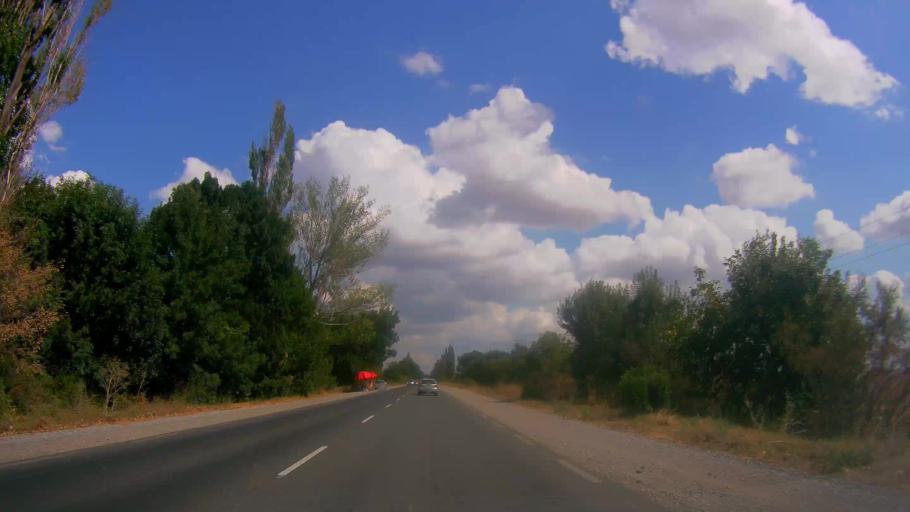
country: BG
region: Sliven
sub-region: Obshtina Sliven
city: Sliven
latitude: 42.6373
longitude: 26.2530
